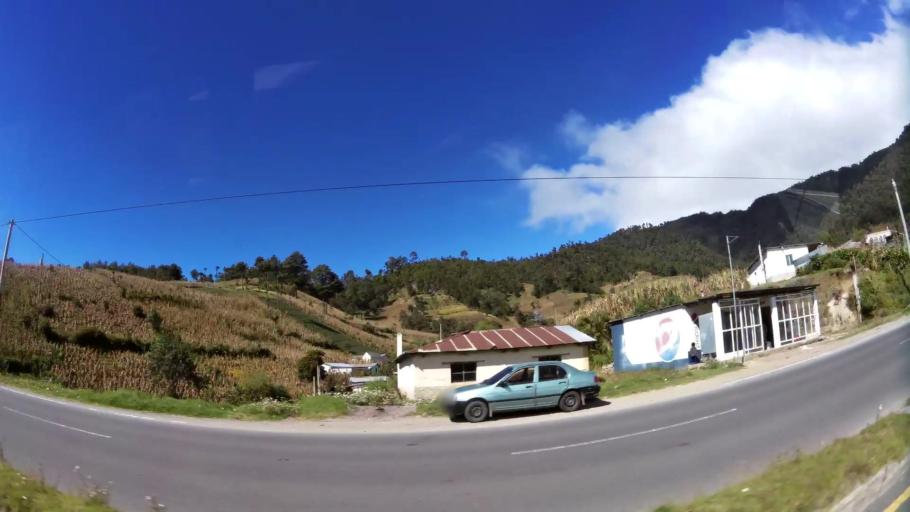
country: GT
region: Solola
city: Concepcion
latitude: 14.8335
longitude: -91.1846
